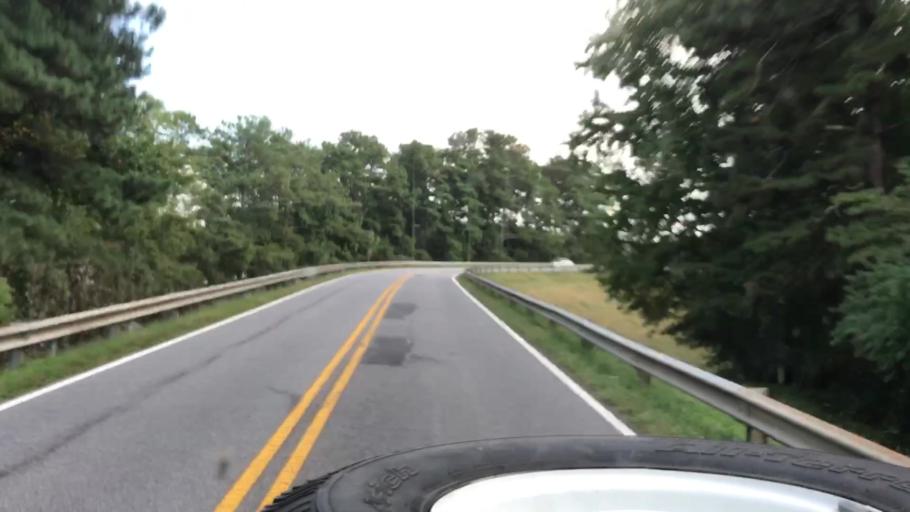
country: US
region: Georgia
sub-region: Forsyth County
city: Cumming
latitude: 34.1740
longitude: -84.0782
